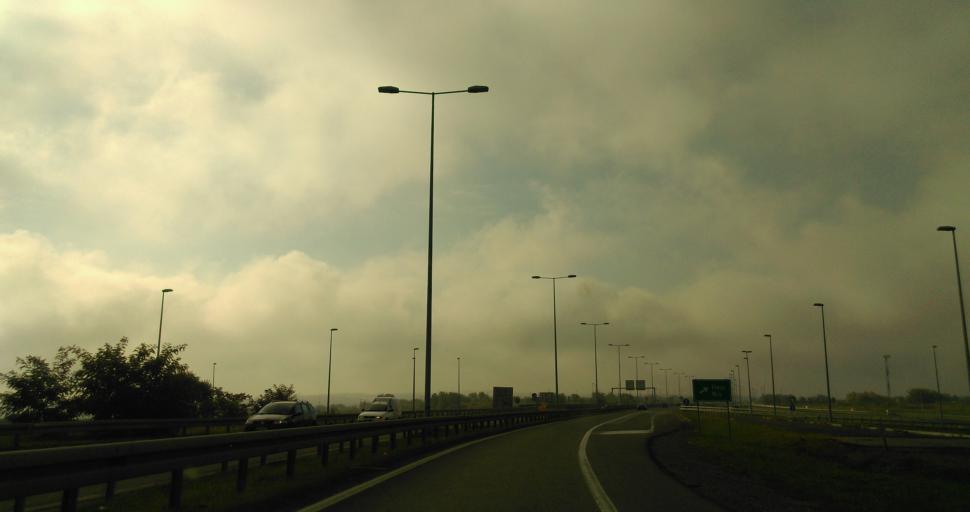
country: RS
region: Central Serbia
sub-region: Belgrade
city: Rakovica
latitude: 44.7156
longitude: 20.4157
